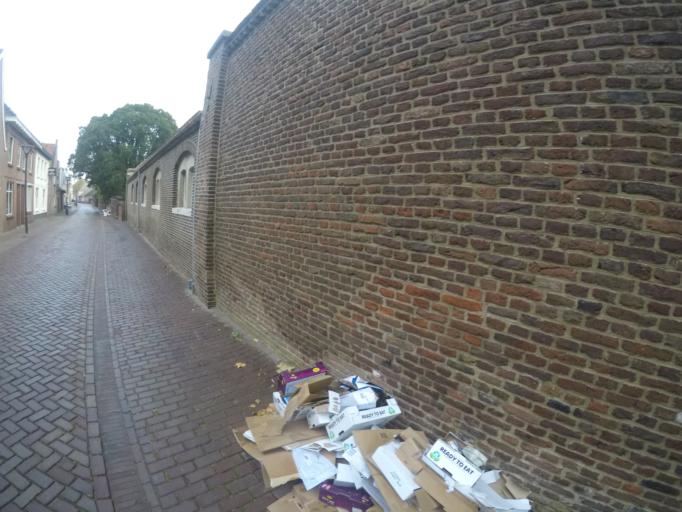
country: NL
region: Gelderland
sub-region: Gemeente Zevenaar
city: Zevenaar
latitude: 51.9265
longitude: 6.0768
